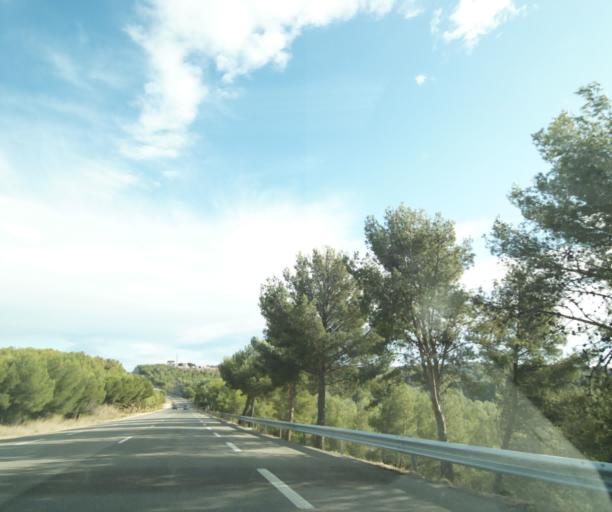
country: FR
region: Provence-Alpes-Cote d'Azur
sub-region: Departement des Bouches-du-Rhone
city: Sausset-les-Pins
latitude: 43.3438
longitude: 5.0913
